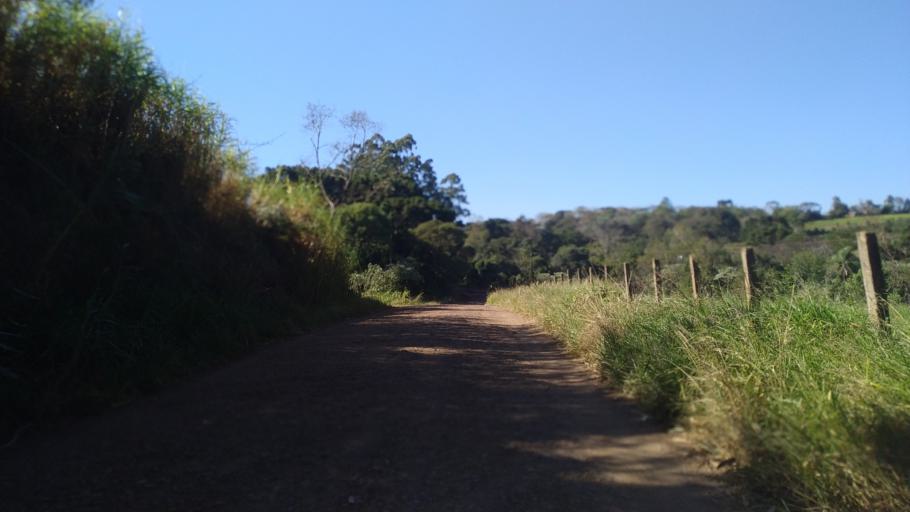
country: BR
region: Santa Catarina
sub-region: Chapeco
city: Chapeco
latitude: -27.1489
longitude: -52.6077
